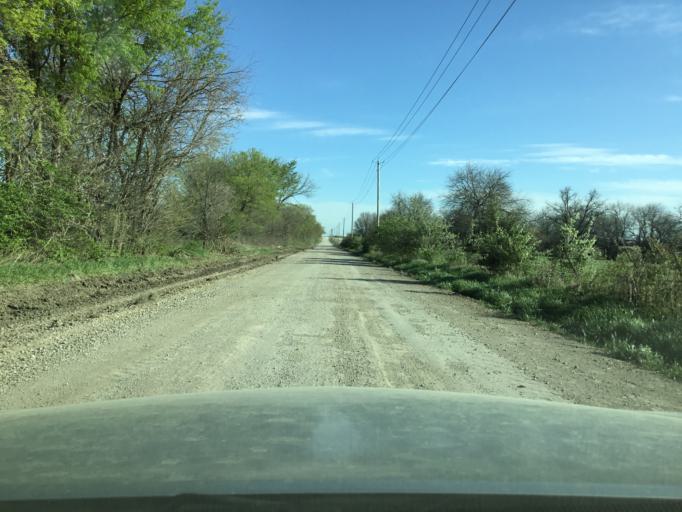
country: US
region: Kansas
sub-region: Neosho County
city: Chanute
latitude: 37.6530
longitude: -95.4893
